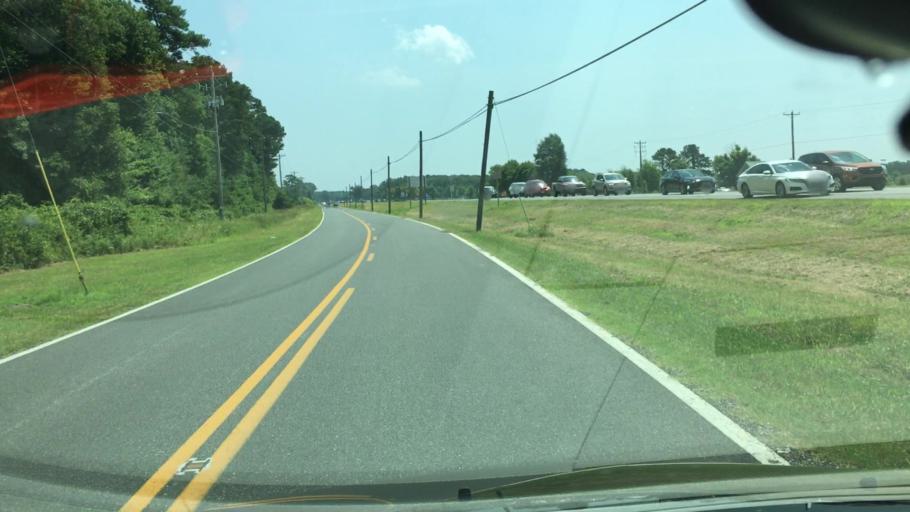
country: US
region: Maryland
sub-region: Worcester County
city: Ocean Pines
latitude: 38.3454
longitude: -75.1648
